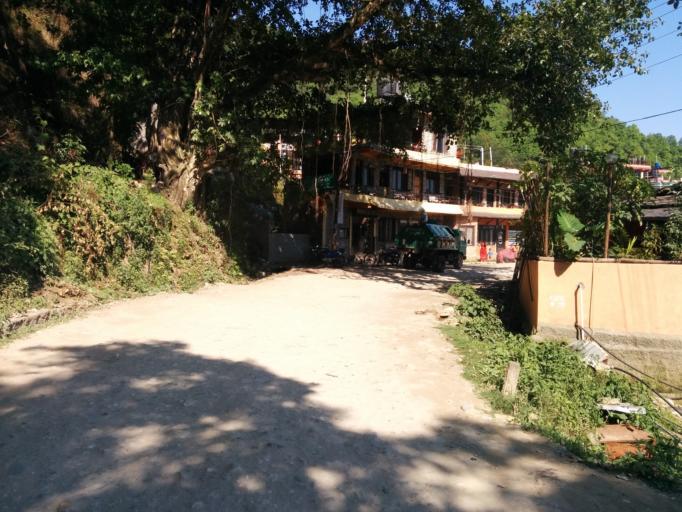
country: NP
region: Western Region
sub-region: Gandaki Zone
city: Pokhara
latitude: 28.2220
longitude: 83.9553
